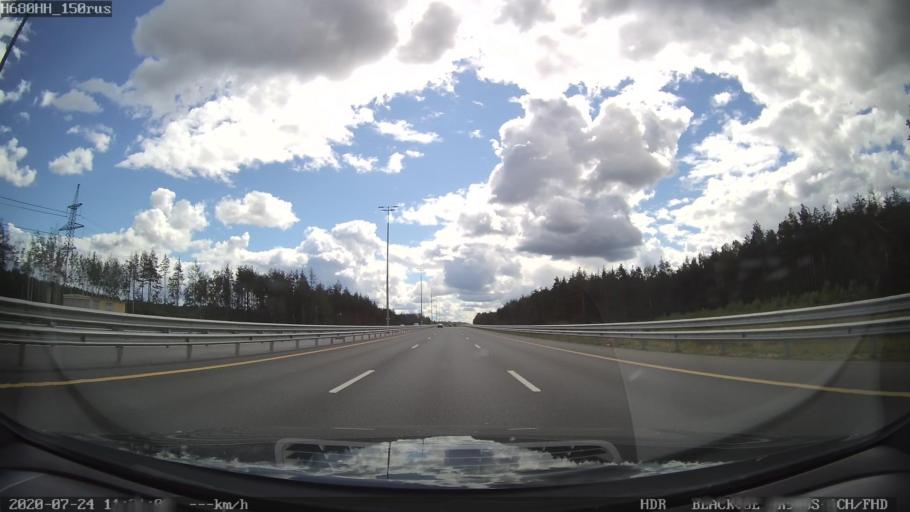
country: RU
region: Leningrad
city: Krasnyy Bor
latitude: 59.6610
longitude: 30.6284
